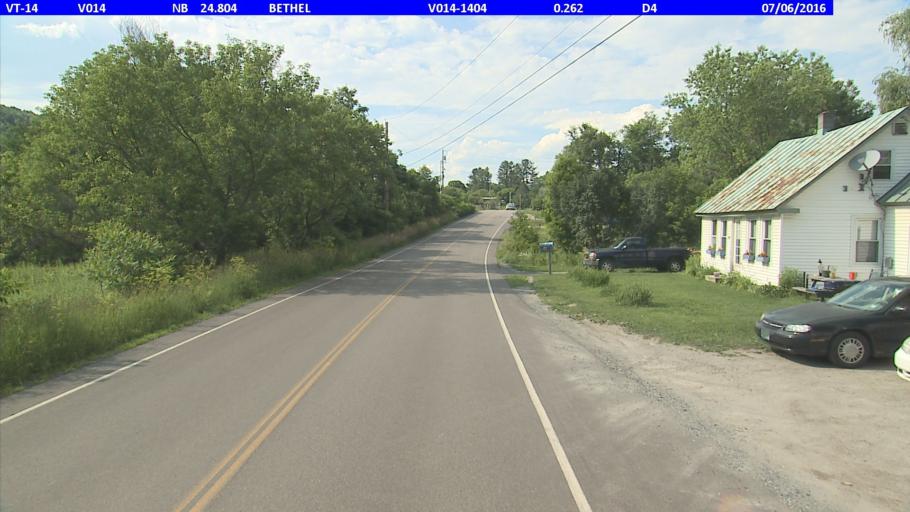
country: US
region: Vermont
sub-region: Orange County
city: Randolph
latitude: 43.8669
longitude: -72.5831
